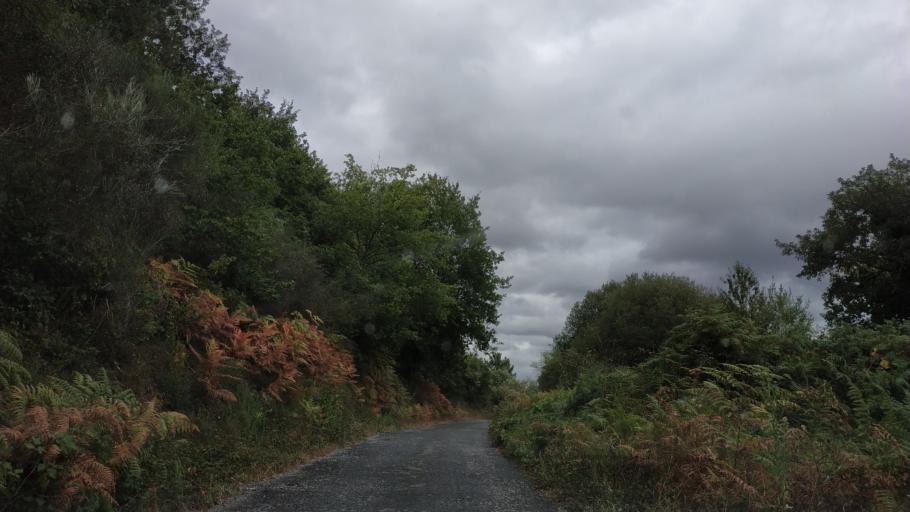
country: ES
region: Galicia
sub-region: Provincia de Lugo
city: Lugo
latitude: 42.9973
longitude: -7.5754
